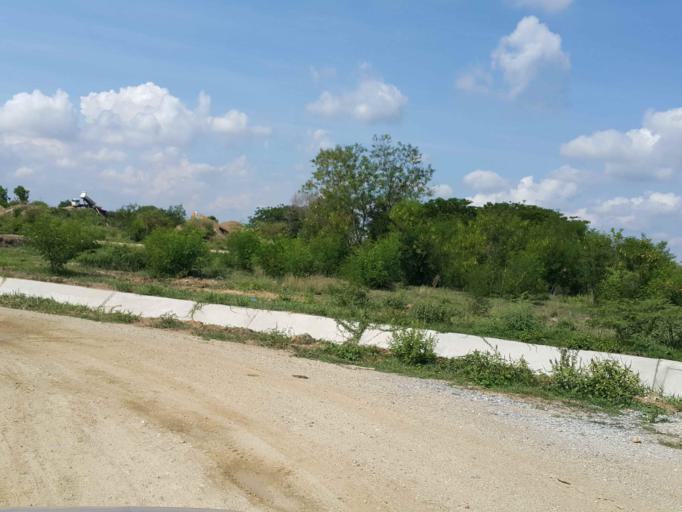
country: TH
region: Chiang Mai
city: San Kamphaeng
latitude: 18.7306
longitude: 99.0890
